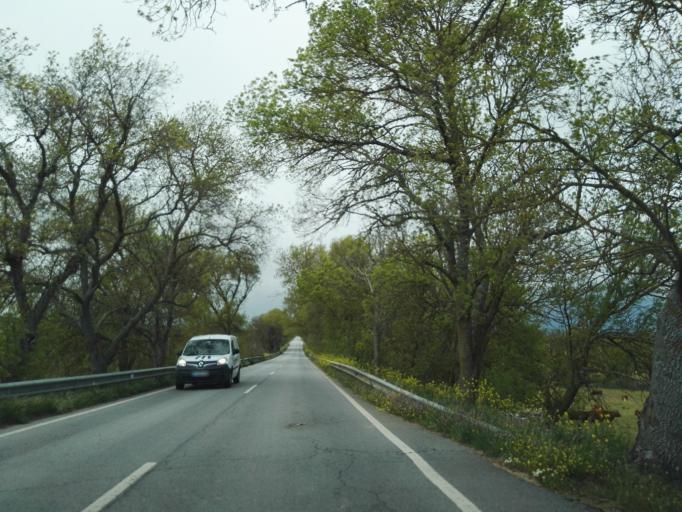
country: PT
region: Portalegre
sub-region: Elvas
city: Elvas
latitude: 38.9590
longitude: -7.2180
